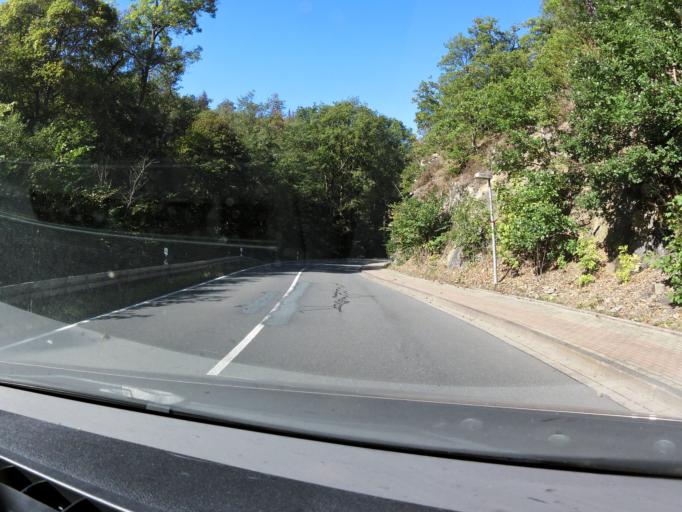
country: DE
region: Saxony-Anhalt
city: Harzgerode
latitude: 51.6664
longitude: 11.1312
